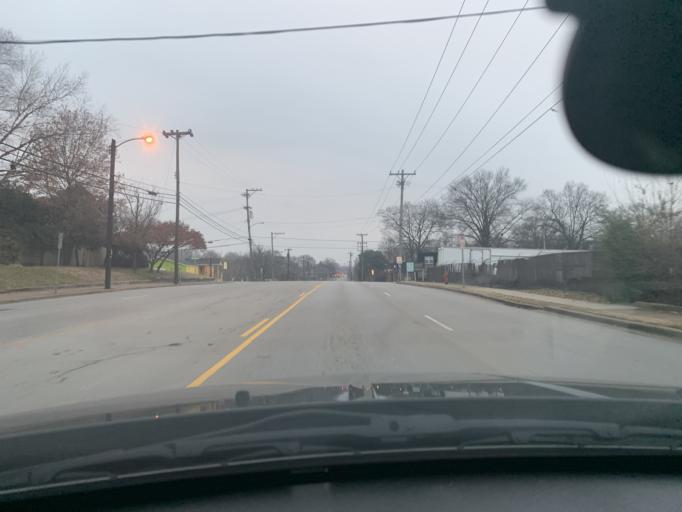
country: US
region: Tennessee
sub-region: Davidson County
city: Nashville
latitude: 36.1705
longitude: -86.7639
